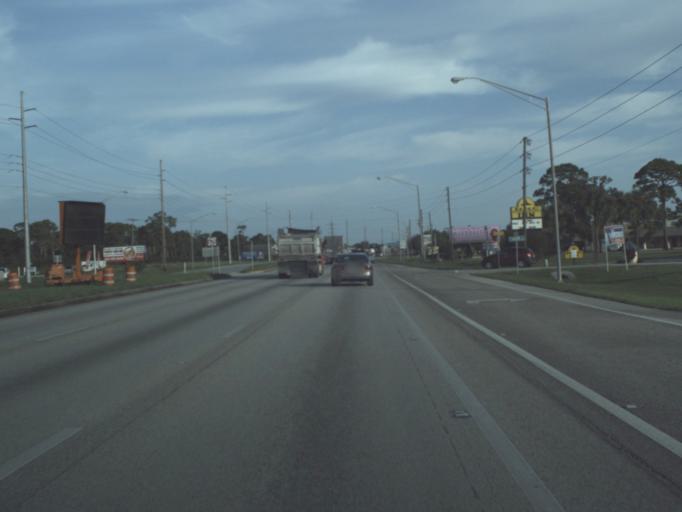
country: US
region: Florida
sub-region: Highlands County
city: Sebring
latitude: 27.4950
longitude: -81.4865
